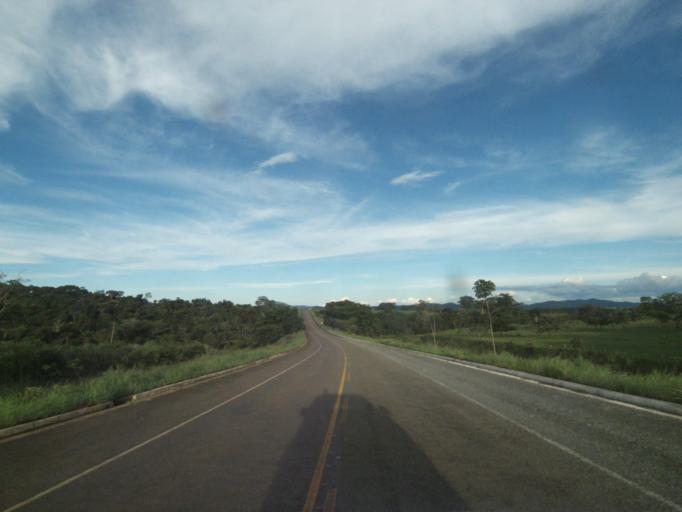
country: BR
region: Goias
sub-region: Jaragua
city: Jaragua
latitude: -15.8399
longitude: -49.2893
